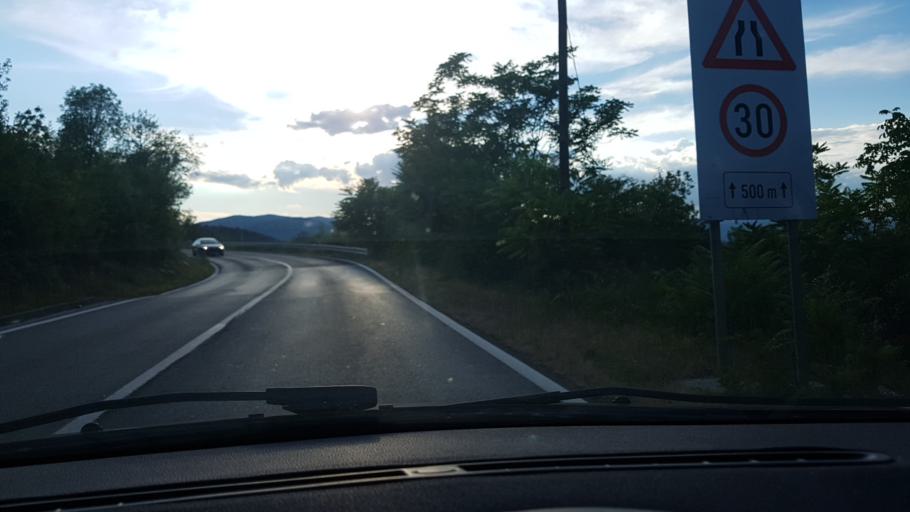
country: HR
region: Splitsko-Dalmatinska
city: Zmijavci
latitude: 43.4305
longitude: 17.1811
